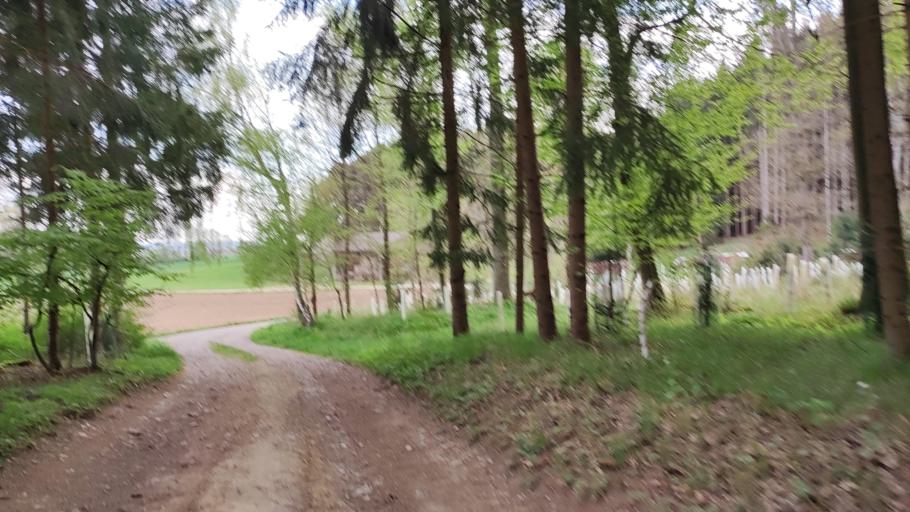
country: DE
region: Bavaria
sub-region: Swabia
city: Zusmarshausen
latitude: 48.3956
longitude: 10.5741
